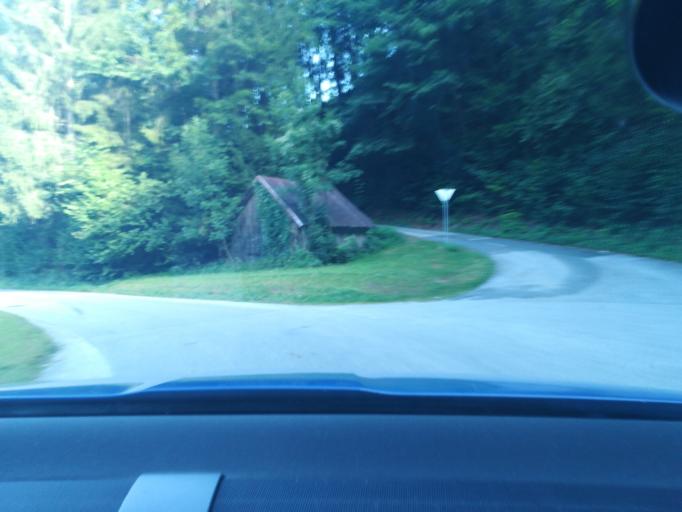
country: AT
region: Salzburg
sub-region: Politischer Bezirk Hallein
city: Abtenau
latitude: 47.5797
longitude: 13.3665
